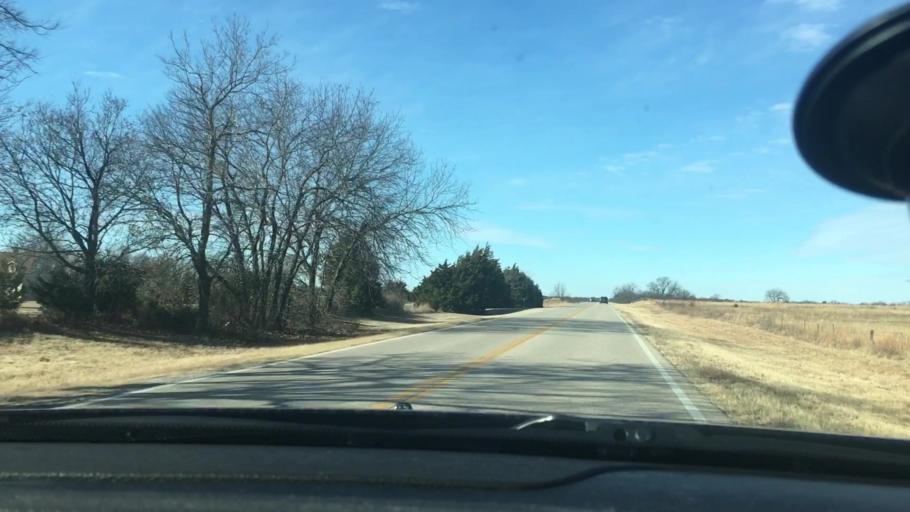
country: US
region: Oklahoma
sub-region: Garvin County
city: Stratford
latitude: 34.9860
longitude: -96.9904
